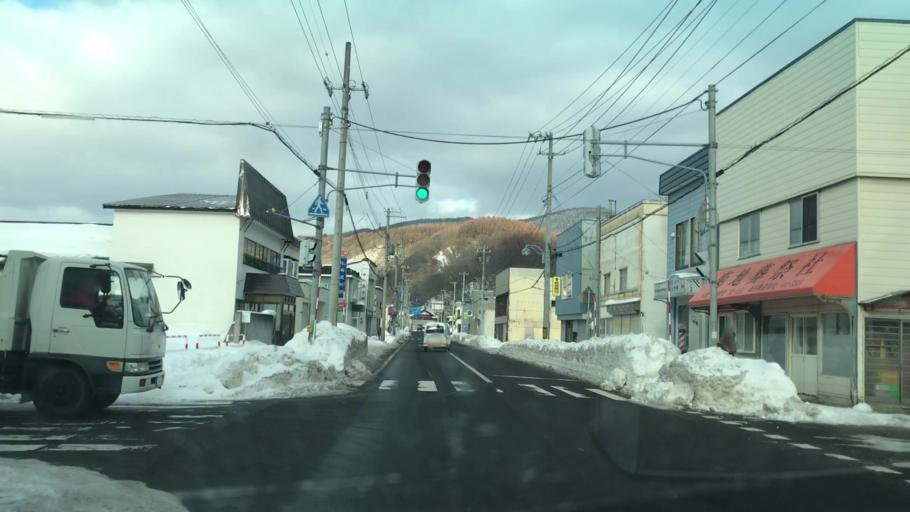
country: JP
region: Hokkaido
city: Yoichi
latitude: 43.2639
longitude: 140.6421
